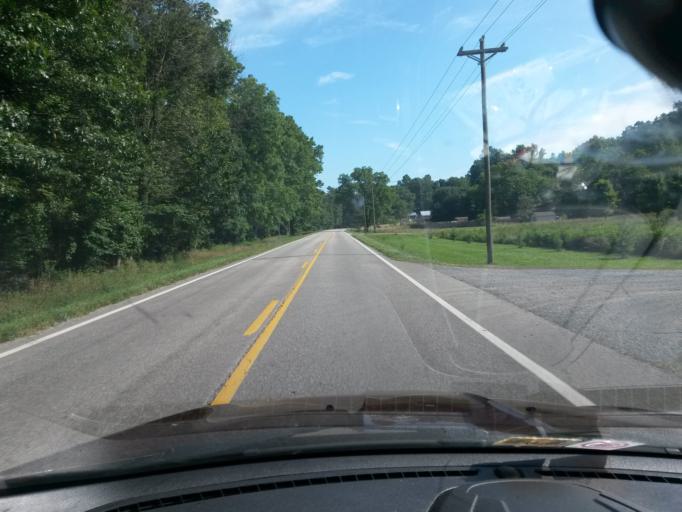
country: US
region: Virginia
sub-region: Shenandoah County
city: Basye
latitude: 38.7197
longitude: -78.9186
